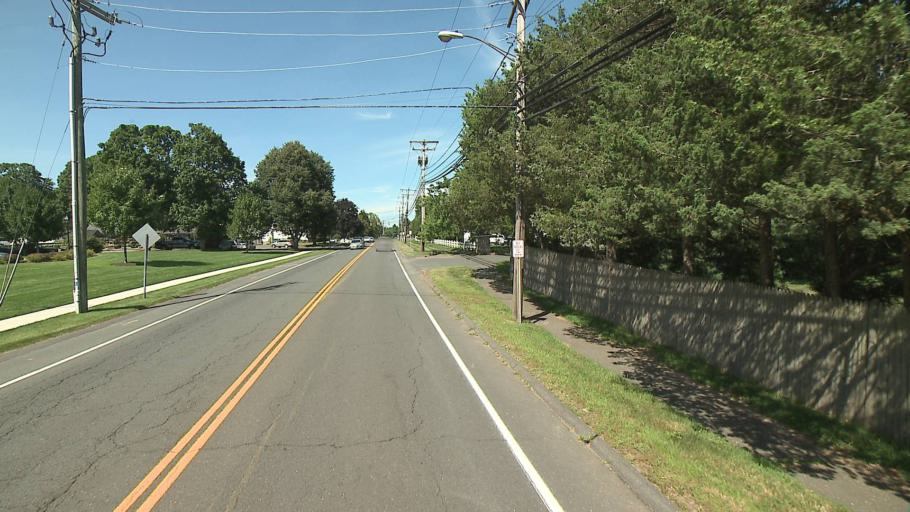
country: US
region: Connecticut
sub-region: Hartford County
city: Canton Valley
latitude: 41.7884
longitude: -72.8636
